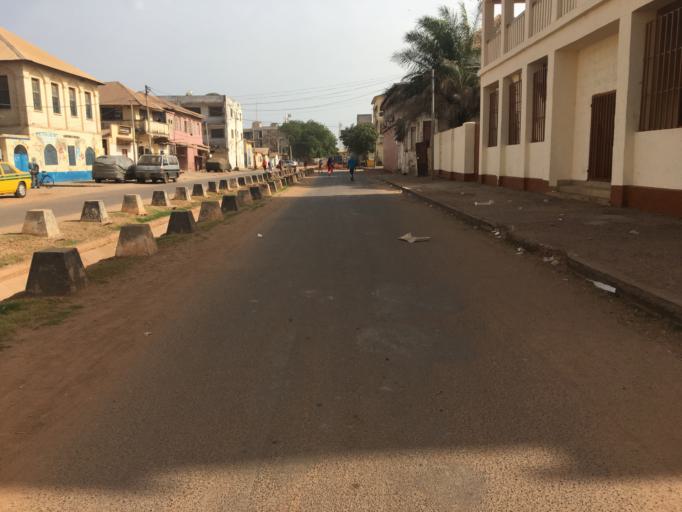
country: GM
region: Banjul
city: Banjul
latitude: 13.4518
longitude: -16.5757
